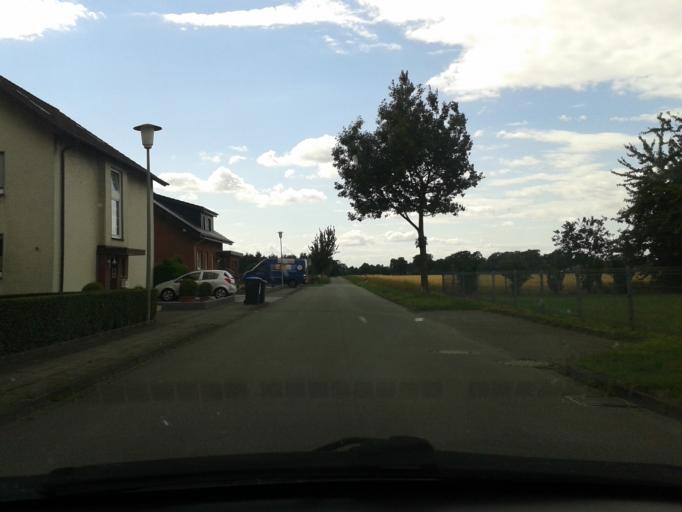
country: DE
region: North Rhine-Westphalia
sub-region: Regierungsbezirk Detmold
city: Paderborn
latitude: 51.7350
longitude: 8.6738
